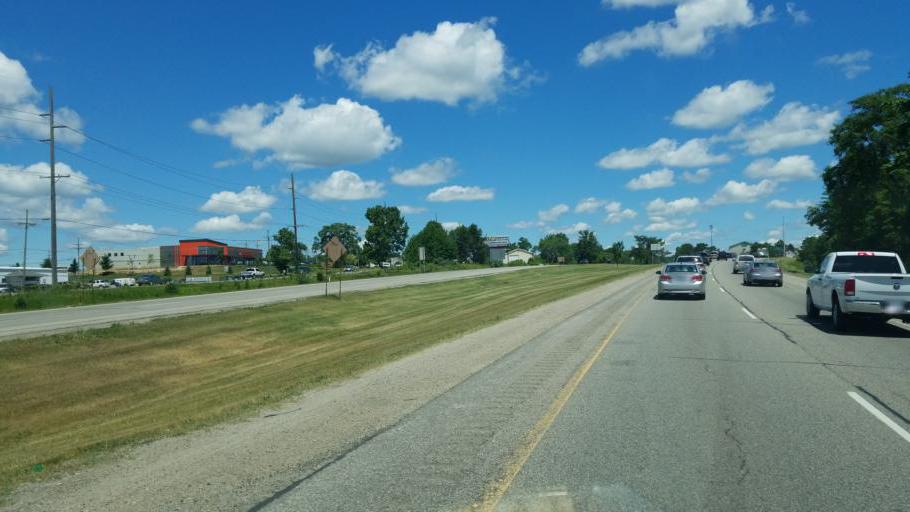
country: US
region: Michigan
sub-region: Livingston County
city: Brighton
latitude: 42.5134
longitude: -83.7582
